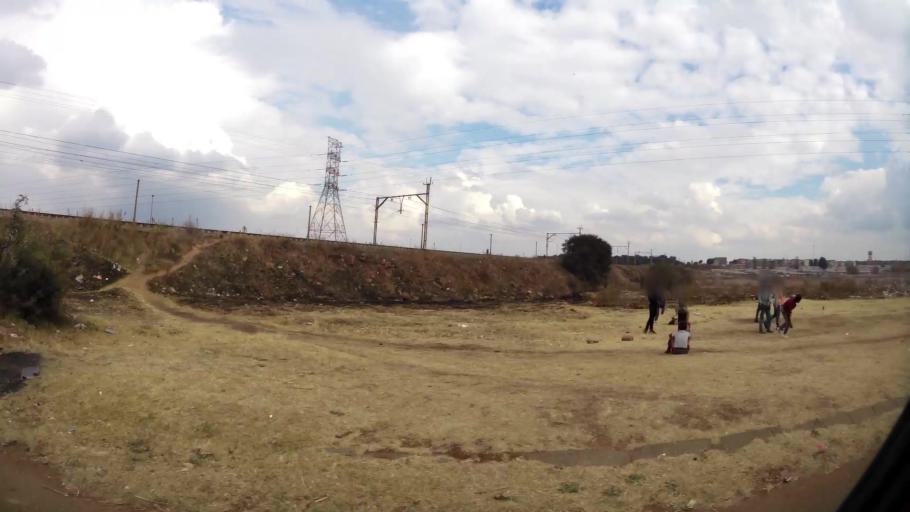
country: ZA
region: Gauteng
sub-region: City of Johannesburg Metropolitan Municipality
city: Soweto
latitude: -26.2377
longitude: 27.8715
